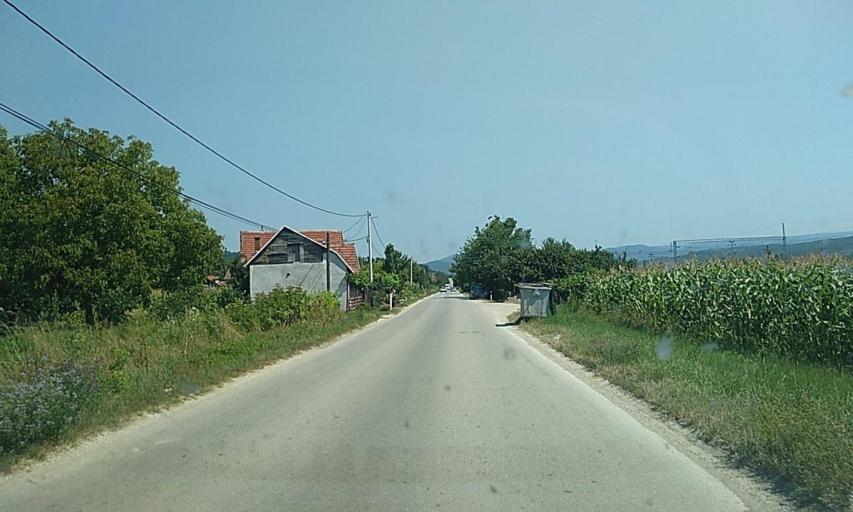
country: RS
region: Central Serbia
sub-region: Pcinjski Okrug
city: Vladicin Han
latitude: 42.6758
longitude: 22.0505
